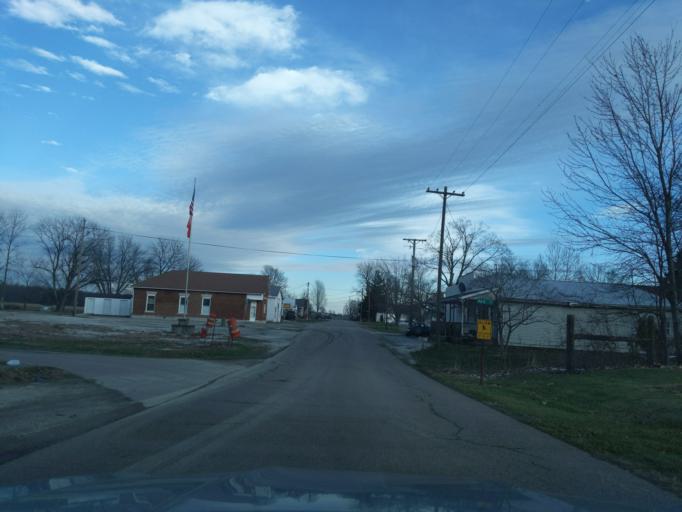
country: US
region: Indiana
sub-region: Decatur County
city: Westport
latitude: 39.2347
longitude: -85.5653
